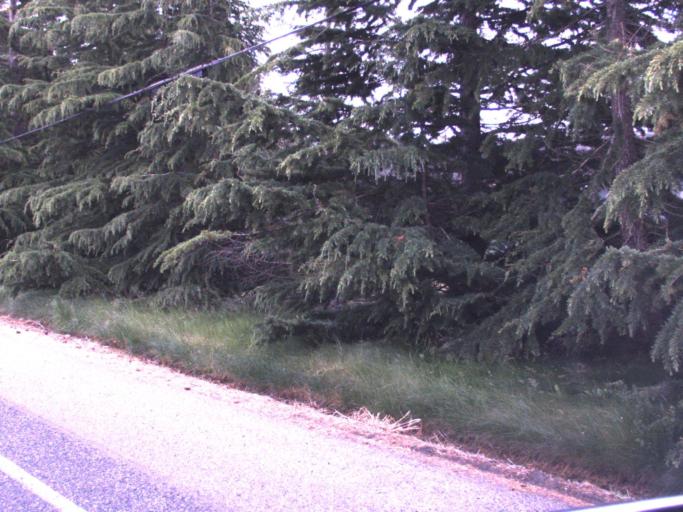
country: US
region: Washington
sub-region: Whatcom County
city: Birch Bay
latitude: 48.8919
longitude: -122.6659
